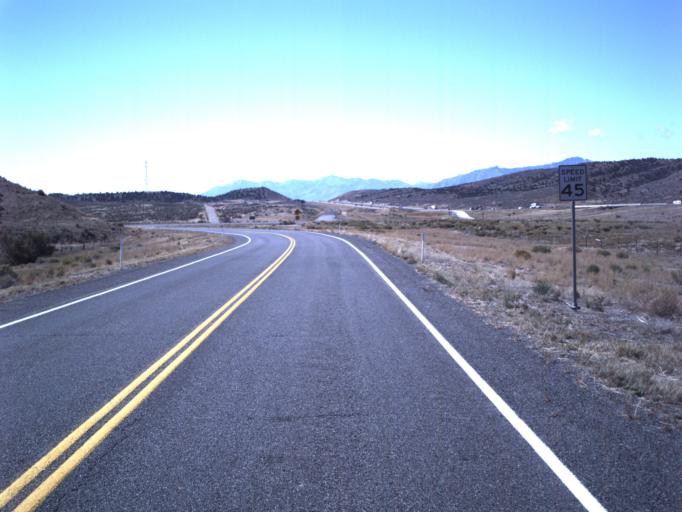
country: US
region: Utah
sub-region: Juab County
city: Nephi
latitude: 39.4849
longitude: -111.9734
